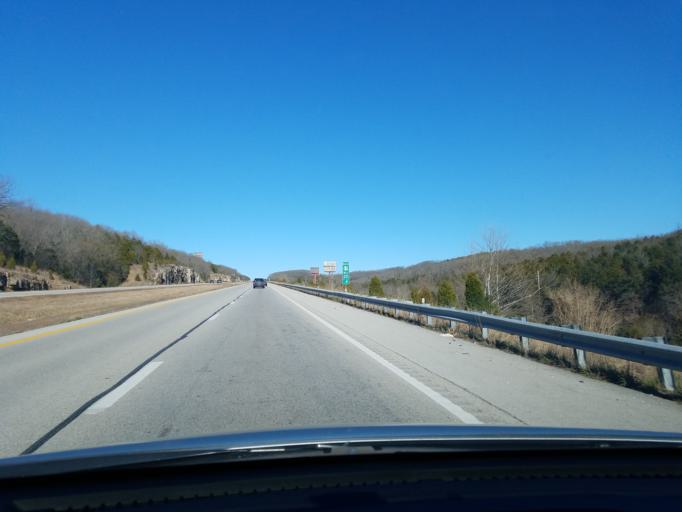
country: US
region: Missouri
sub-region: Taney County
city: Merriam Woods
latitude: 36.7725
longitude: -93.2242
